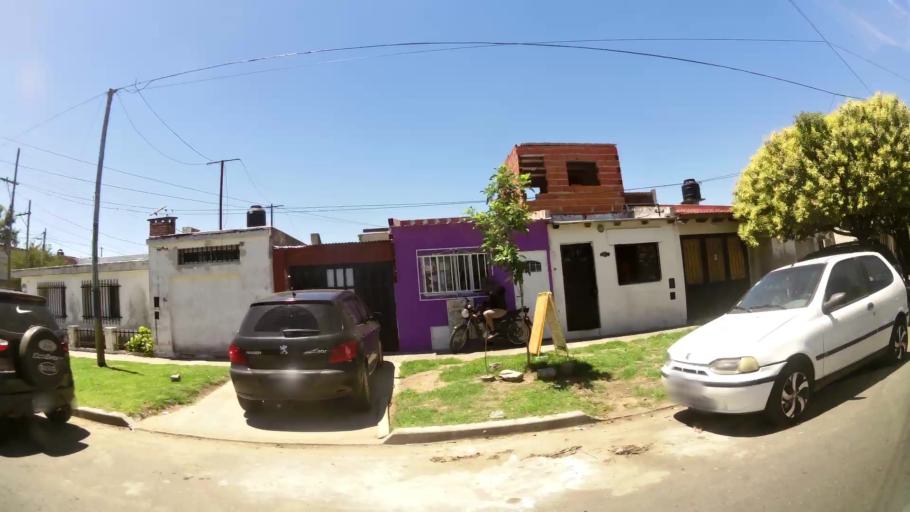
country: AR
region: Santa Fe
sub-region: Departamento de Rosario
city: Rosario
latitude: -32.9512
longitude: -60.7098
